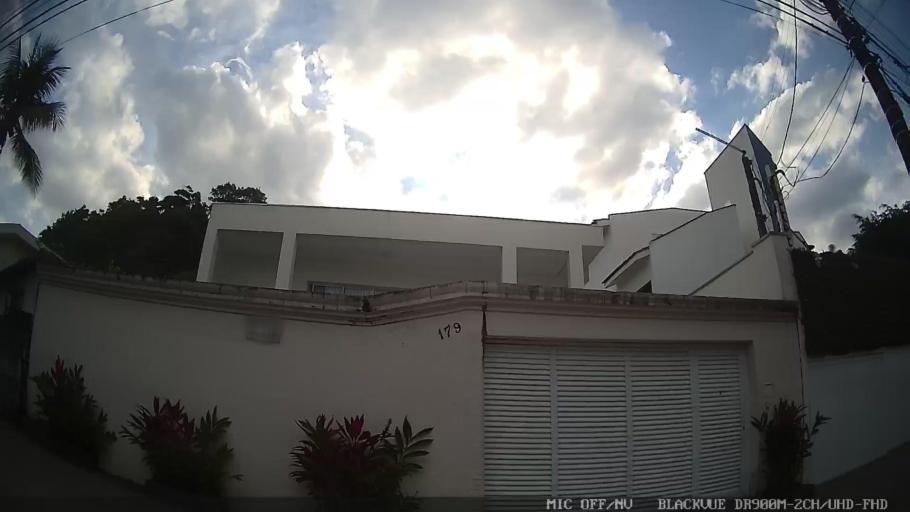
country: BR
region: Sao Paulo
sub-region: Guaruja
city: Guaruja
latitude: -23.9866
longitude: -46.2390
